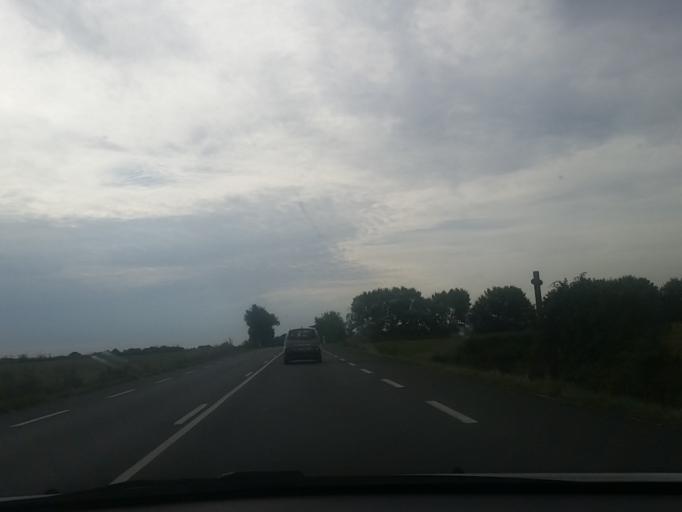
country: FR
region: Pays de la Loire
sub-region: Departement de la Vendee
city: Saint-Fulgent
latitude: 46.8811
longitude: -1.2098
